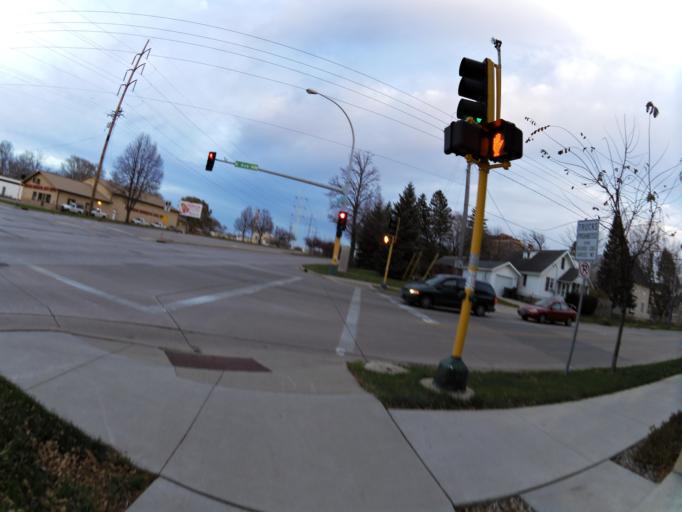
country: US
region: Minnesota
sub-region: Olmsted County
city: Rochester
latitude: 44.0279
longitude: -92.4712
